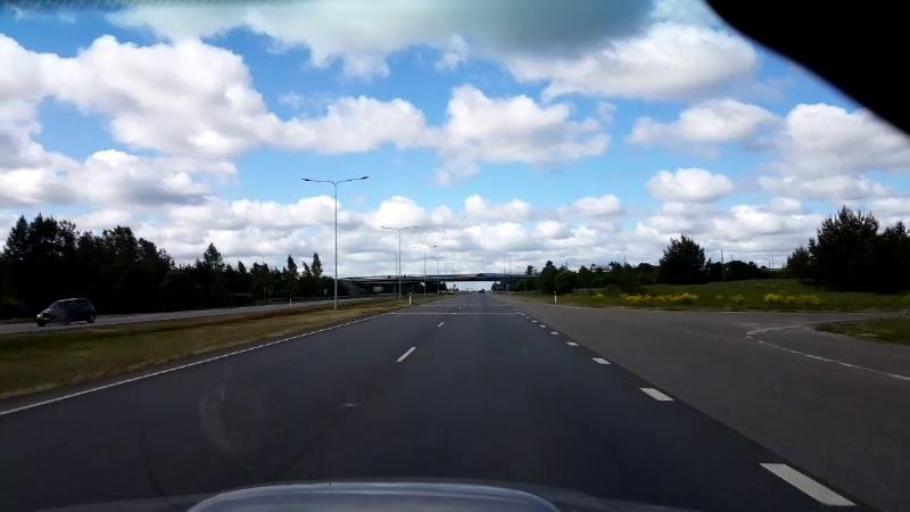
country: EE
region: Harju
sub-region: Saue linn
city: Saue
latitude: 59.3126
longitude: 24.5740
